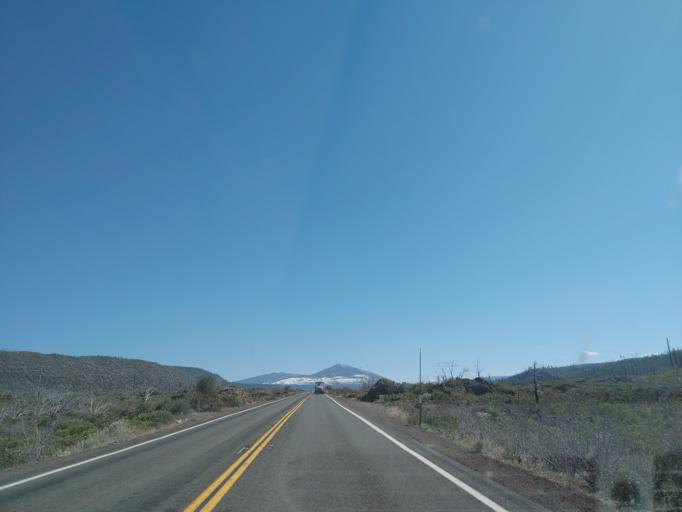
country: US
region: California
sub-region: Shasta County
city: Burney
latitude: 40.7221
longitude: -121.4258
